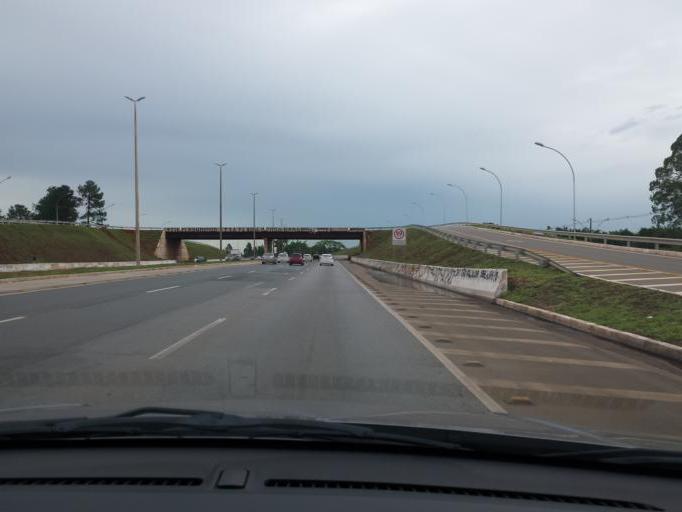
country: BR
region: Federal District
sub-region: Brasilia
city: Brasilia
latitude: -15.9083
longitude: -47.9655
